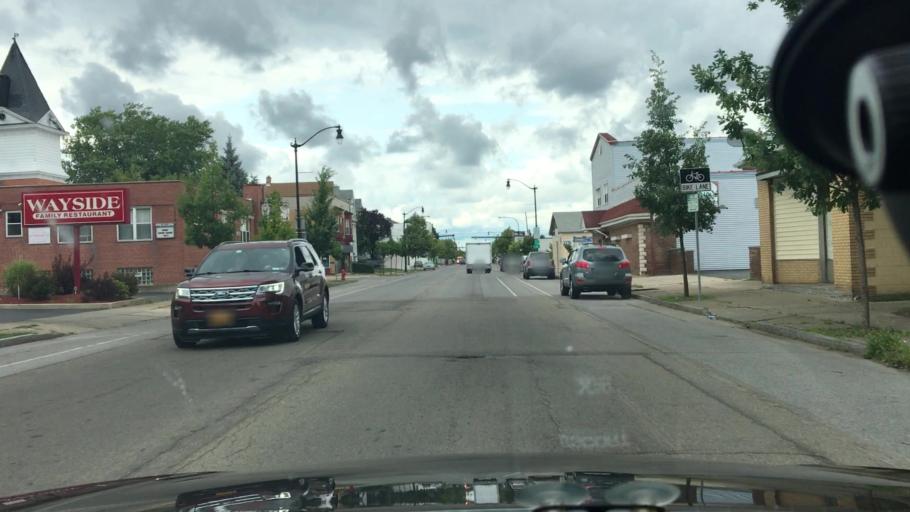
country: US
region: New York
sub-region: Erie County
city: Lackawanna
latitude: 42.8357
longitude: -78.8238
